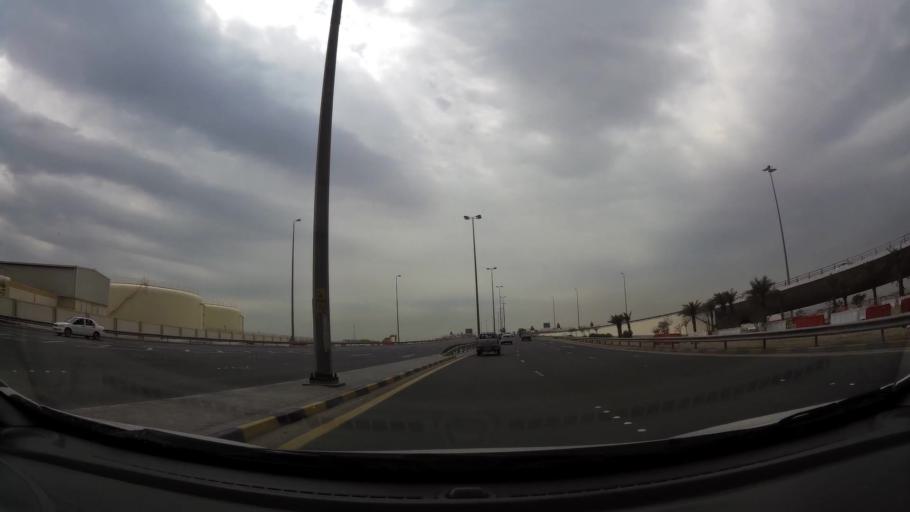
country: BH
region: Manama
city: Manama
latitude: 26.1973
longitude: 50.5904
